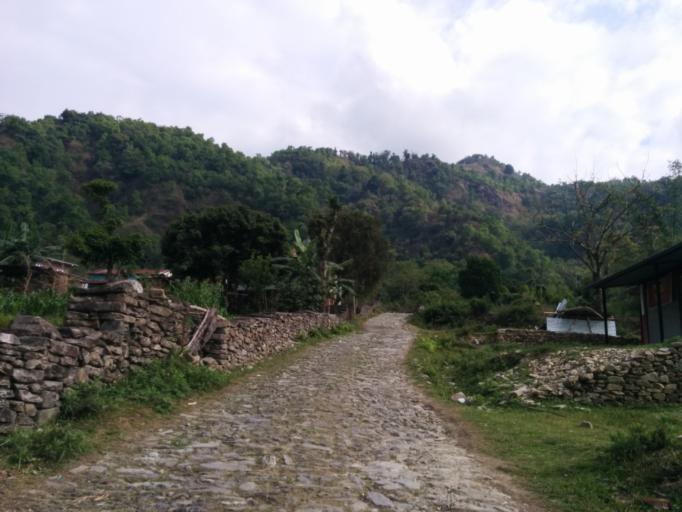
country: NP
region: Western Region
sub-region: Gandaki Zone
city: Pokhara
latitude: 28.2288
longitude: 83.9494
